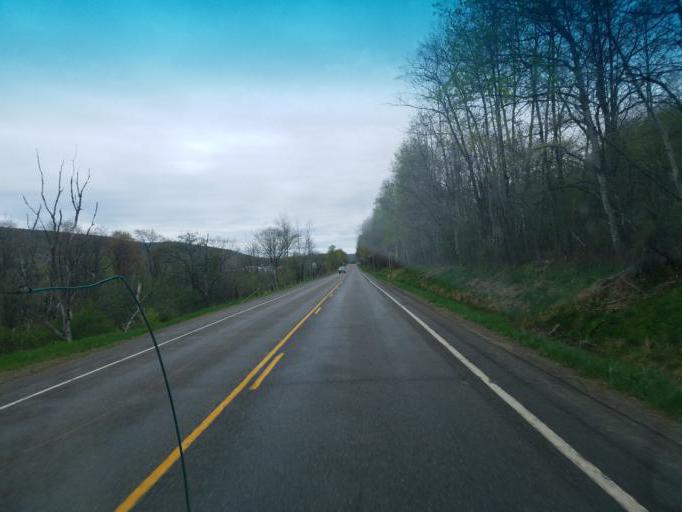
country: US
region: New York
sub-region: Allegany County
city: Andover
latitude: 42.0165
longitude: -77.8307
